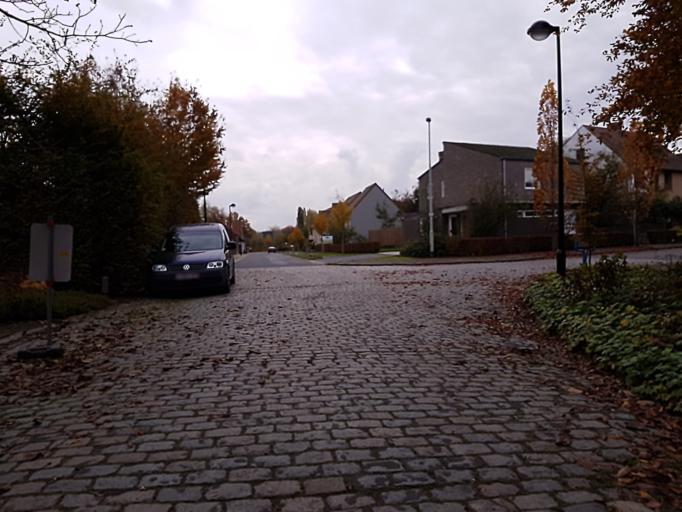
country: BE
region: Flanders
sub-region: Provincie Antwerpen
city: Hove
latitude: 51.1499
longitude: 4.4749
